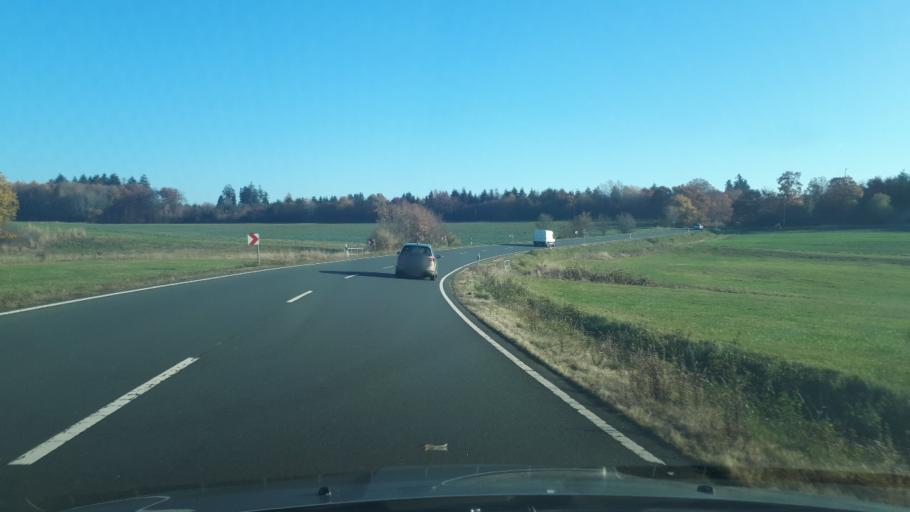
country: DE
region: Rheinland-Pfalz
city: Buchel
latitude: 50.1684
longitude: 7.0938
